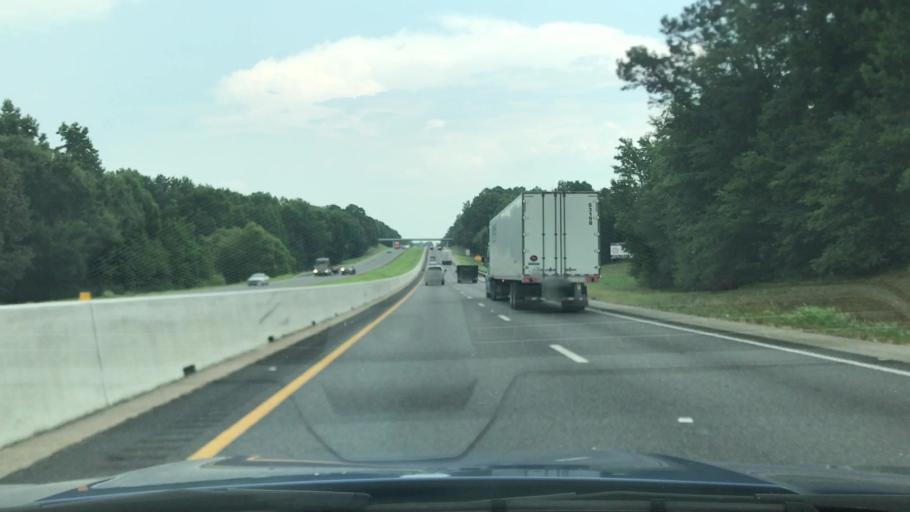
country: US
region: Texas
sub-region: Gregg County
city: Liberty City
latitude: 32.4360
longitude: -94.9781
